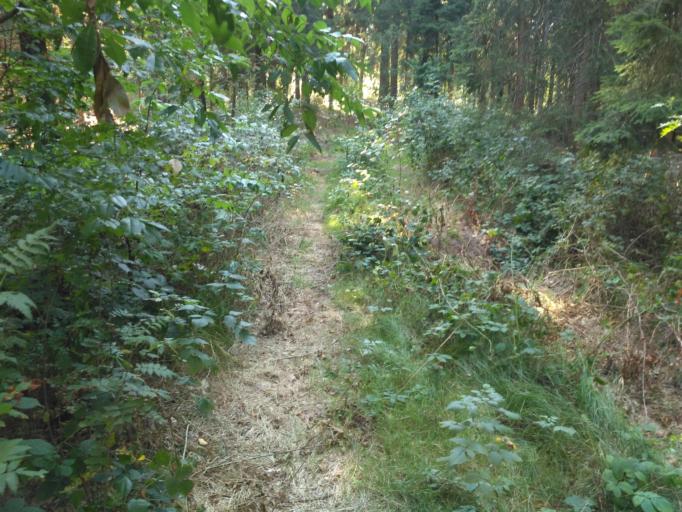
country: DE
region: Saxony
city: Coswig
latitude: 51.1562
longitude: 13.6146
